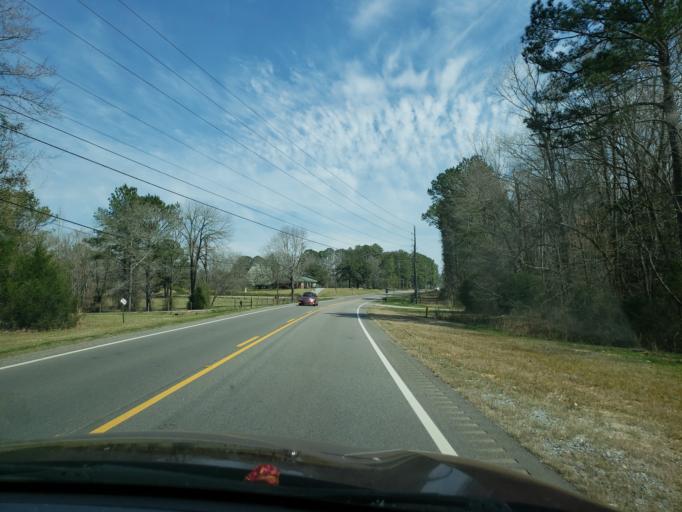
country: US
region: Alabama
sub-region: Elmore County
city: Eclectic
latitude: 32.5813
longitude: -86.0848
